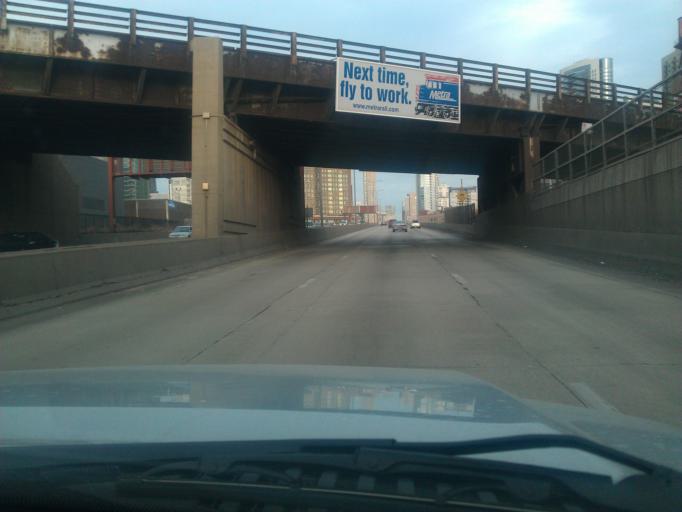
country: US
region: Illinois
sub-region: Cook County
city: Chicago
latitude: 41.8924
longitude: -87.6477
